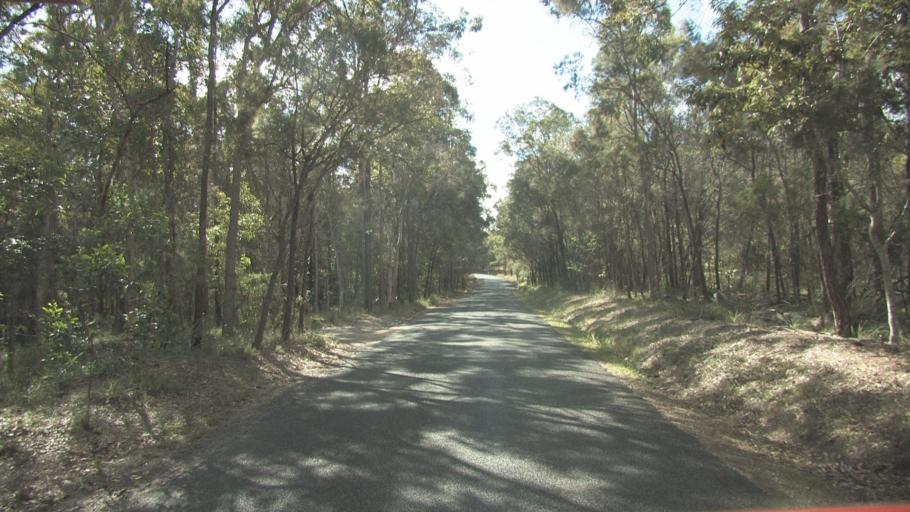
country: AU
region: Queensland
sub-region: Logan
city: Beenleigh
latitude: -27.6536
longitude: 153.2299
